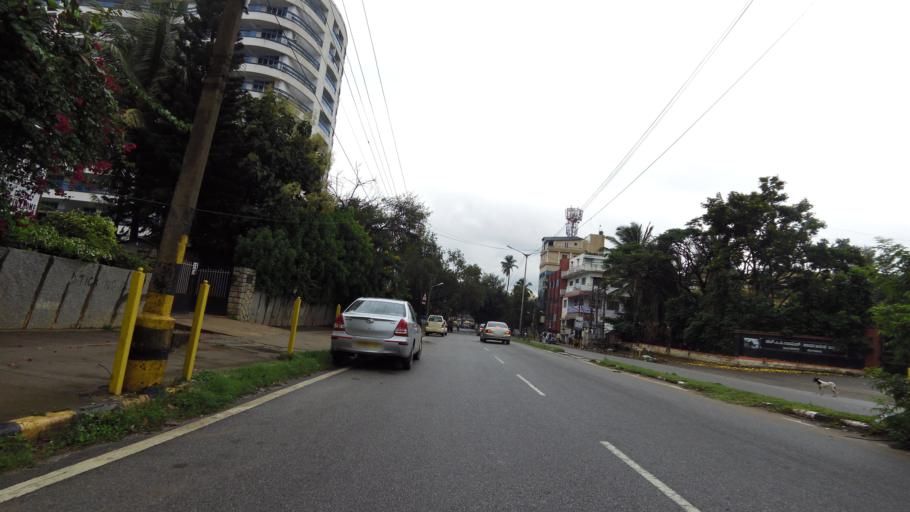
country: IN
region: Karnataka
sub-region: Bangalore Urban
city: Bangalore
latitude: 12.9829
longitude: 77.6457
